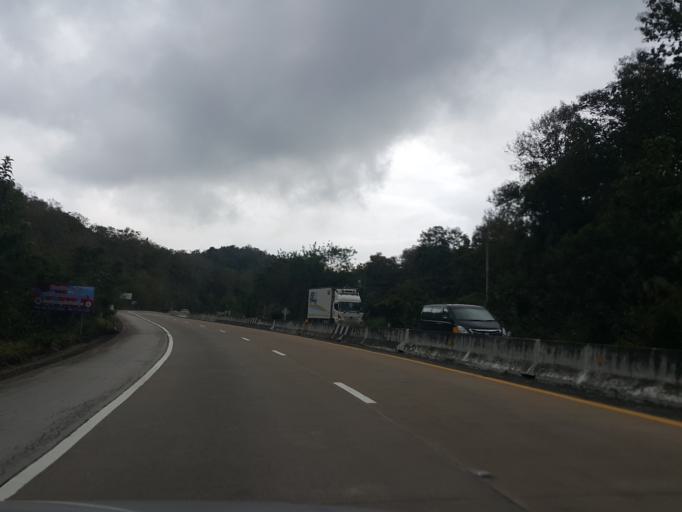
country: TH
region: Lampang
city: Hang Chat
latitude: 18.3463
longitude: 99.2443
